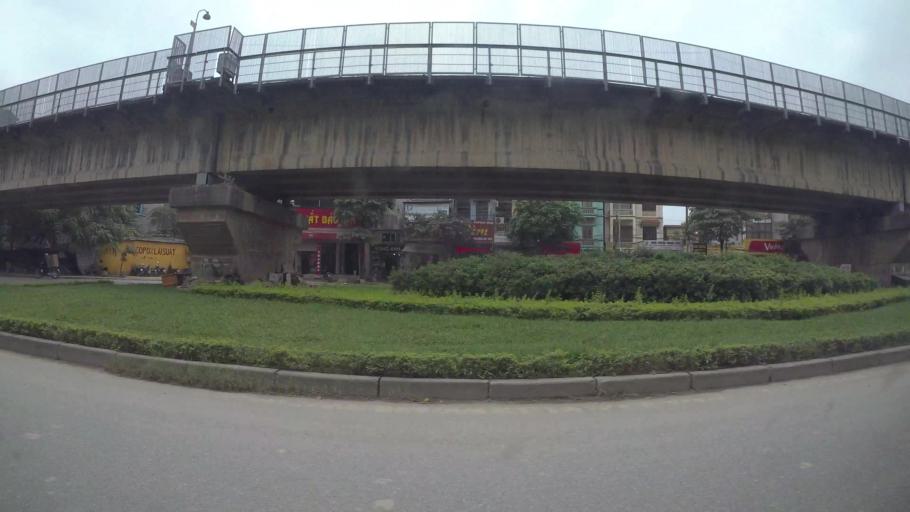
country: VN
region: Ha Noi
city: Tay Ho
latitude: 21.0807
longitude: 105.7853
